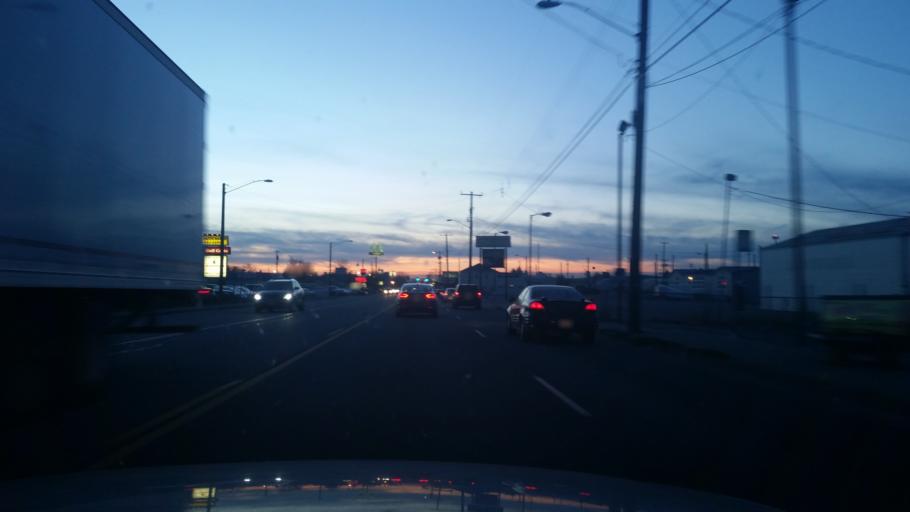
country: US
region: Washington
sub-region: Spokane County
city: Millwood
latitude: 47.6573
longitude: -117.3425
